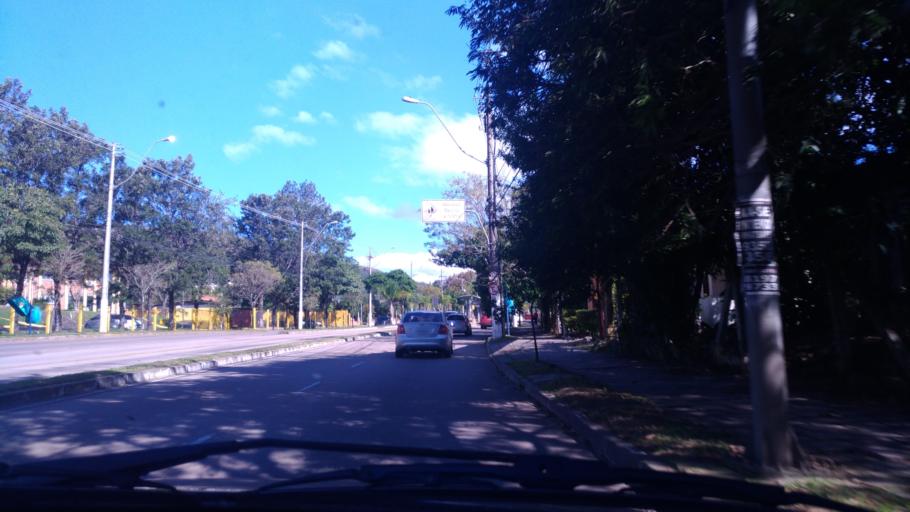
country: BR
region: Rio Grande do Sul
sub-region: Porto Alegre
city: Porto Alegre
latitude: -30.0670
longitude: -51.1871
